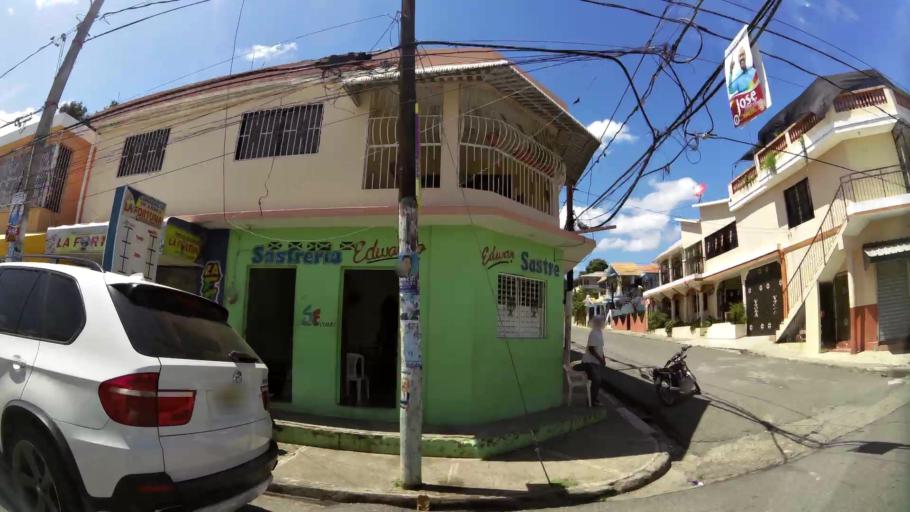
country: DO
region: San Cristobal
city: San Cristobal
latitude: 18.4051
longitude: -70.1119
